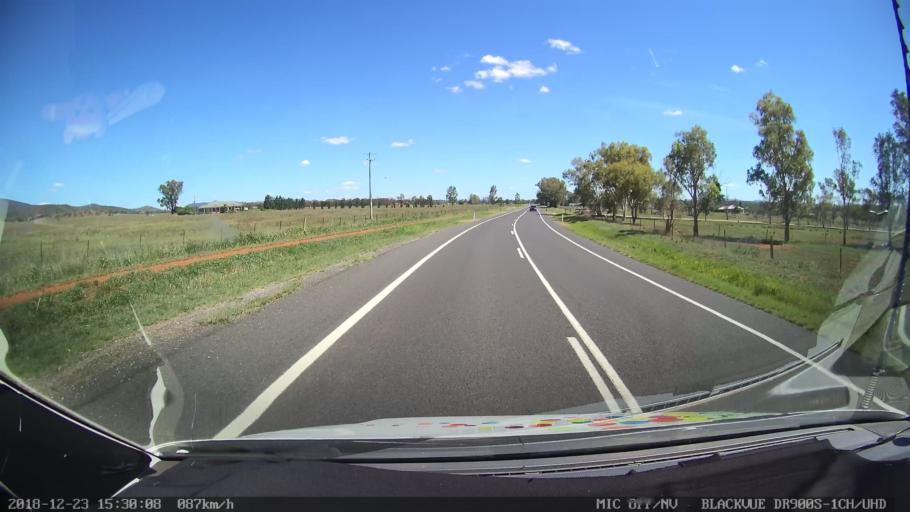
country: AU
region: New South Wales
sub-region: Tamworth Municipality
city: East Tamworth
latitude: -30.9547
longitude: 150.8662
